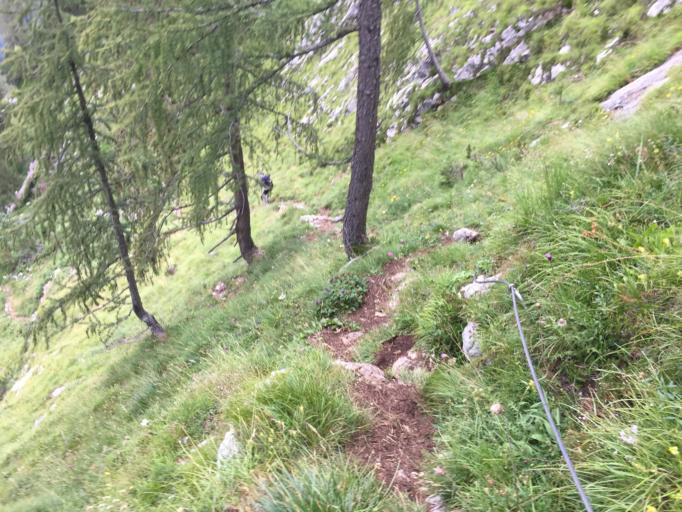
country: IT
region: Friuli Venezia Giulia
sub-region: Provincia di Udine
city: Forni Avoltri
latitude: 46.5656
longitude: 12.7645
